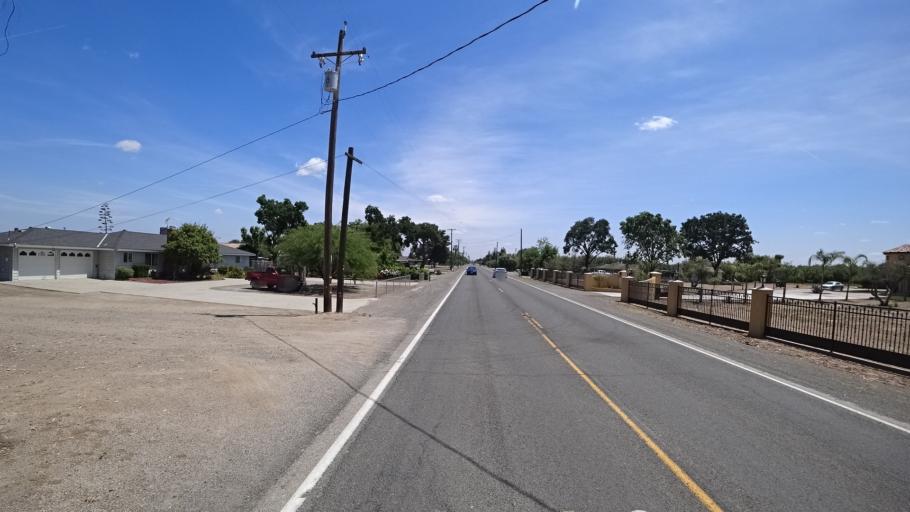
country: US
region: California
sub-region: Kings County
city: Armona
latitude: 36.2988
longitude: -119.7425
